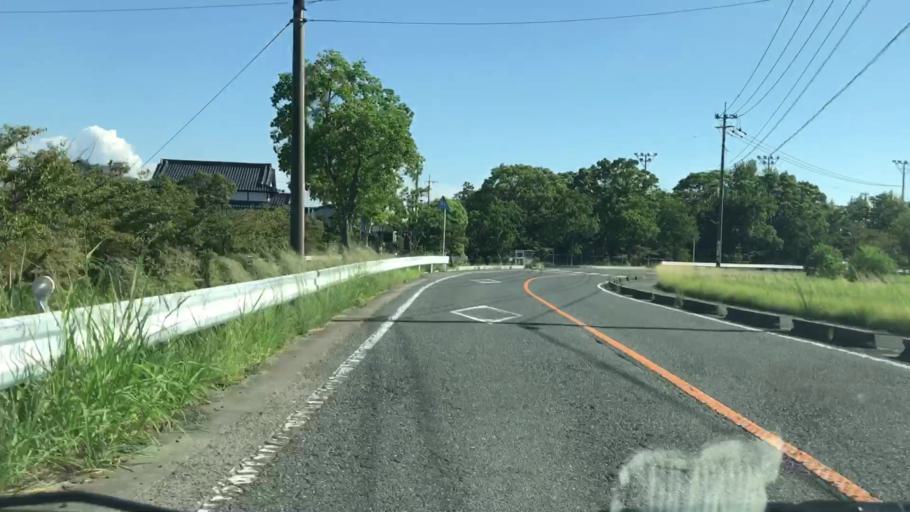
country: JP
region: Saga Prefecture
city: Okawa
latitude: 33.2283
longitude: 130.3559
